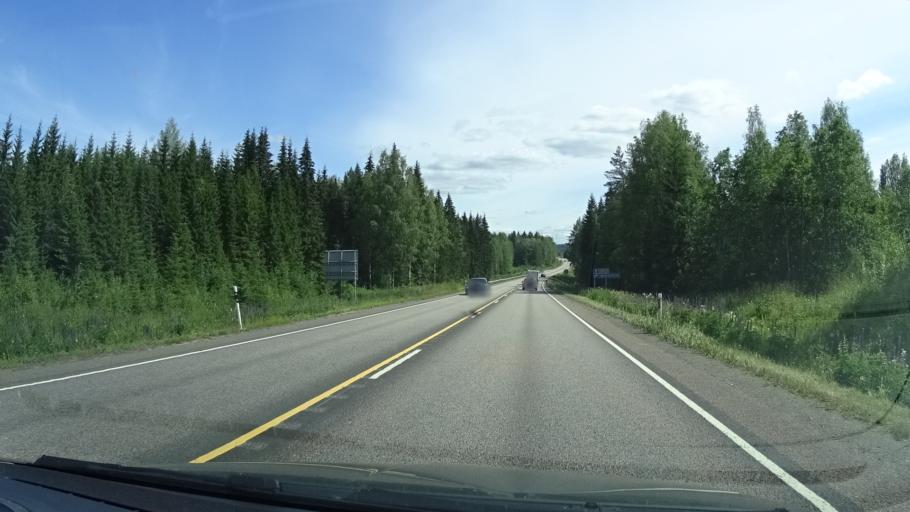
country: FI
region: Central Finland
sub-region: Jyvaeskylae
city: Uurainen
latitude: 62.2666
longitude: 25.4379
